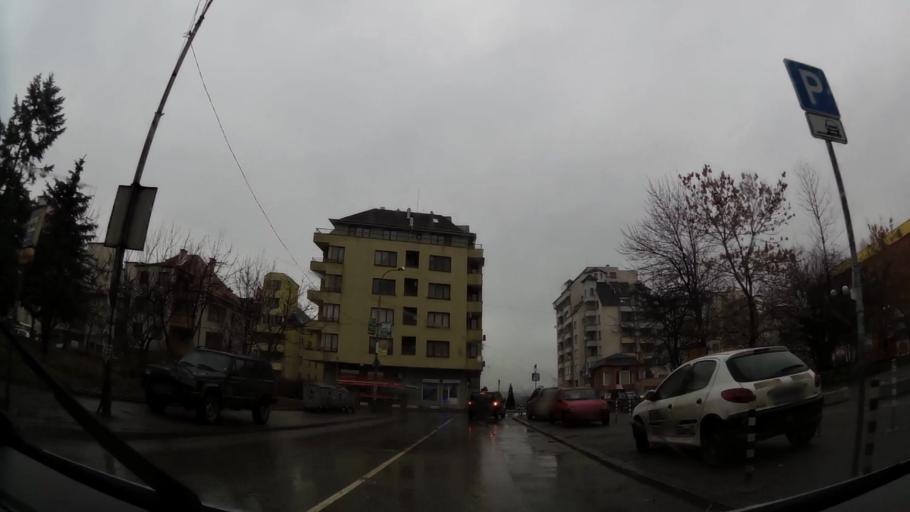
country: BG
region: Sofia-Capital
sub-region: Stolichna Obshtina
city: Sofia
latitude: 42.6425
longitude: 23.3670
